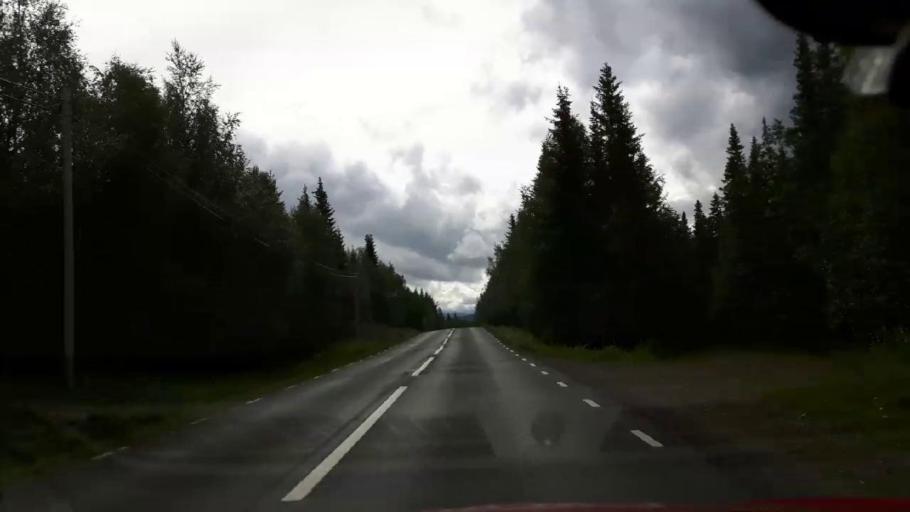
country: NO
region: Nord-Trondelag
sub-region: Lierne
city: Sandvika
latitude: 64.5217
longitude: 14.1636
